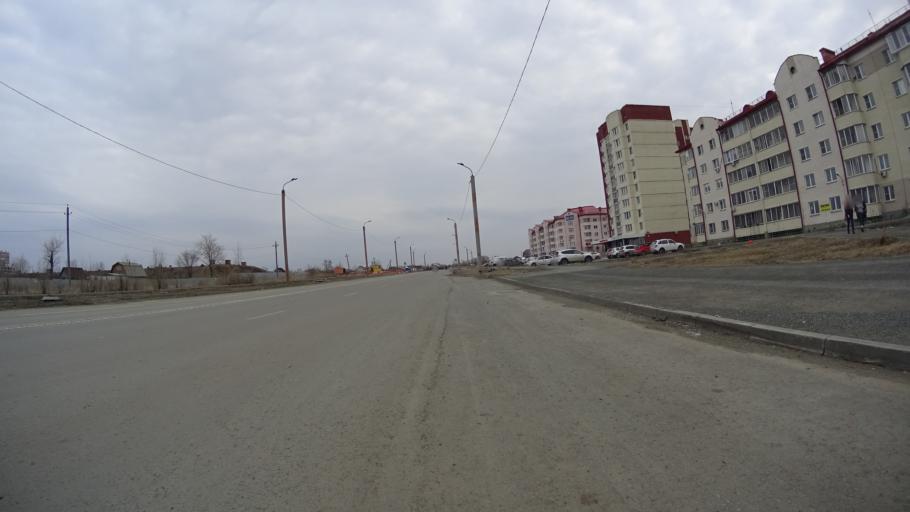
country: RU
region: Chelyabinsk
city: Zheleznodorozhnyy
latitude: 55.1705
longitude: 61.5379
